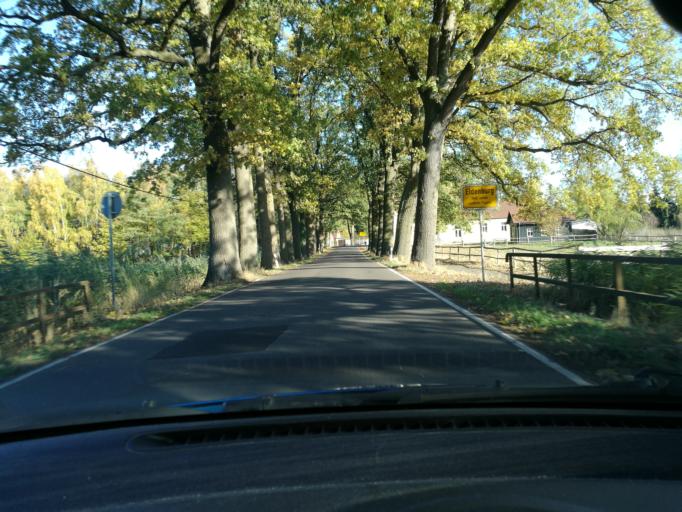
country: DE
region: Brandenburg
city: Lenzen
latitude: 53.1135
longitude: 11.4369
